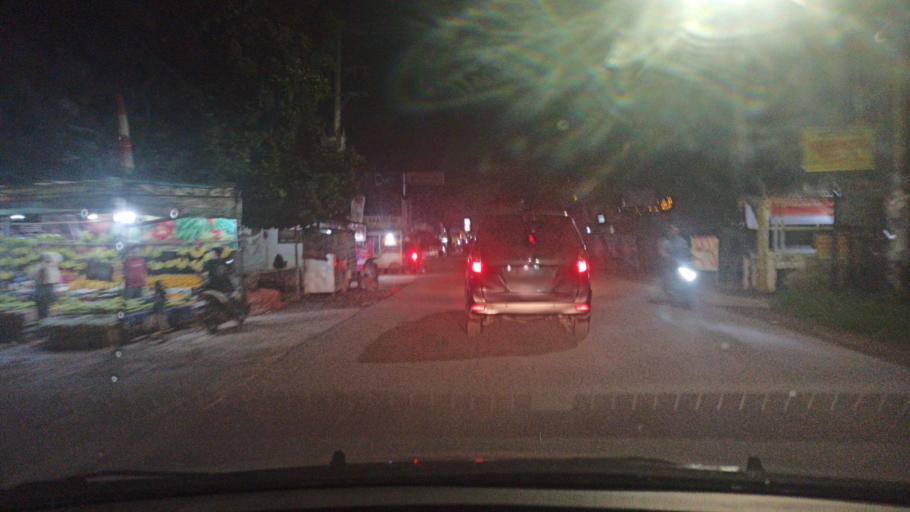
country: ID
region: South Sumatra
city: Palembang
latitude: -2.9420
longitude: 104.7838
